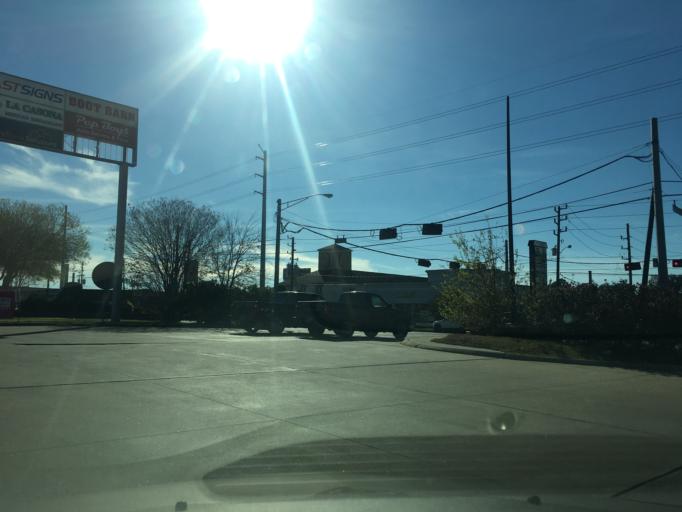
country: US
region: Texas
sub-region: Fort Bend County
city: Rosenberg
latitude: 29.5345
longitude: -95.8079
